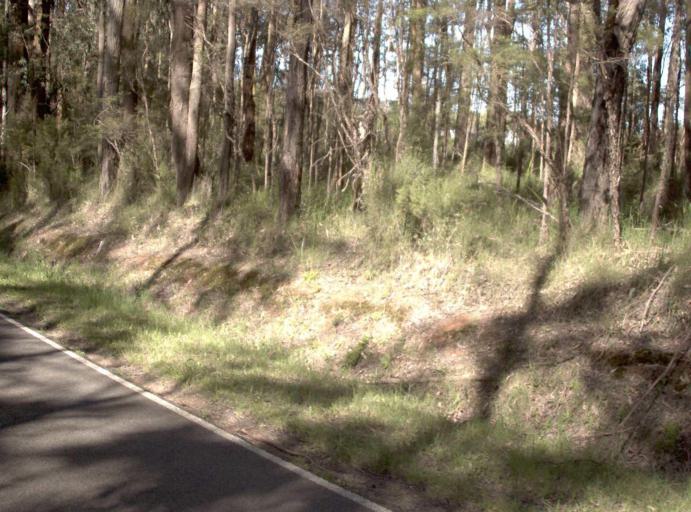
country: AU
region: Victoria
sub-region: Baw Baw
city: Warragul
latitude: -37.8909
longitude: 145.9287
